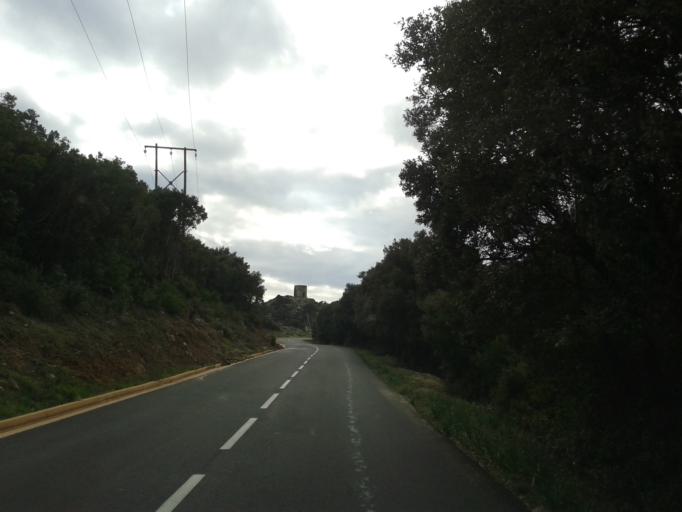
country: FR
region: Corsica
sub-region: Departement de la Haute-Corse
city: Brando
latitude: 42.9736
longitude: 9.3723
